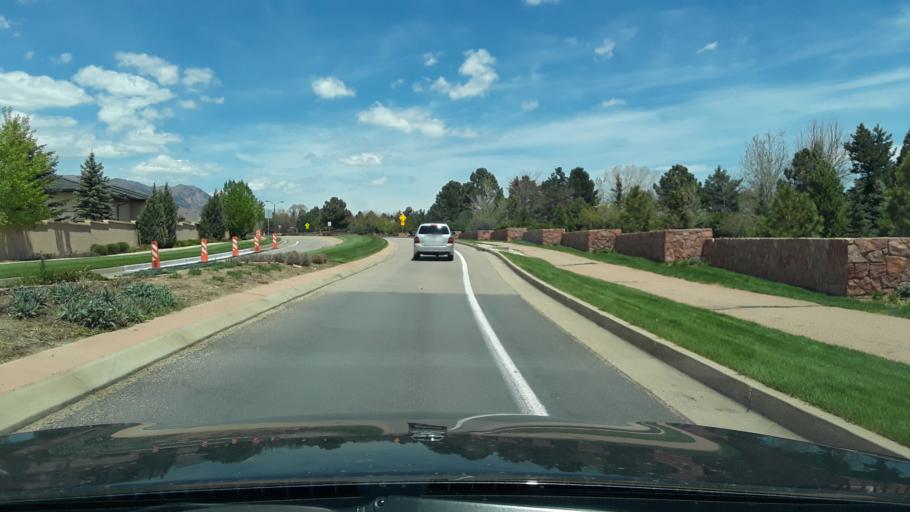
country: US
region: Colorado
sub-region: El Paso County
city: Manitou Springs
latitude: 38.8763
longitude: -104.8651
